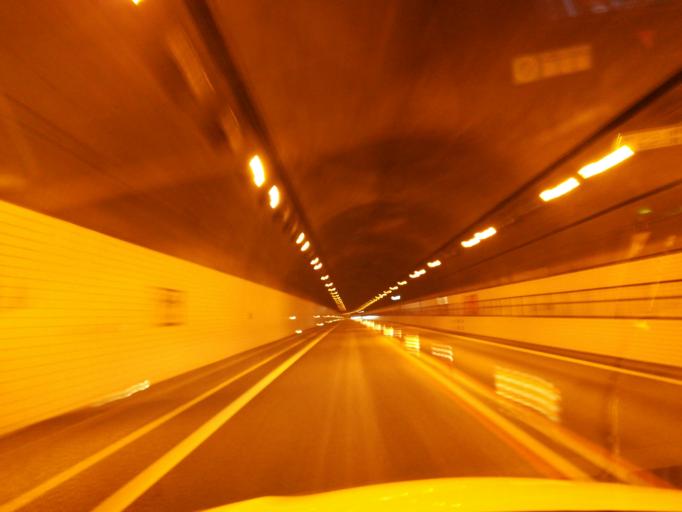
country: JP
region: Tokushima
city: Ikedacho
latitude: 34.0215
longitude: 133.8021
